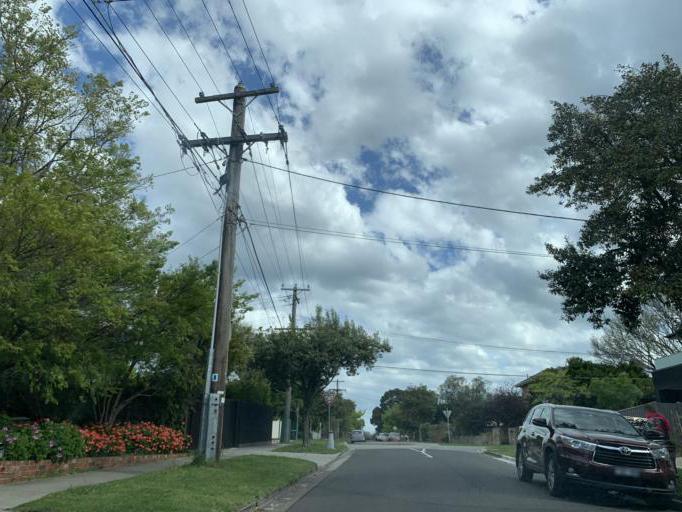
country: AU
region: Victoria
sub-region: Bayside
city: Hampton
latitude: -37.9262
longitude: 145.0119
